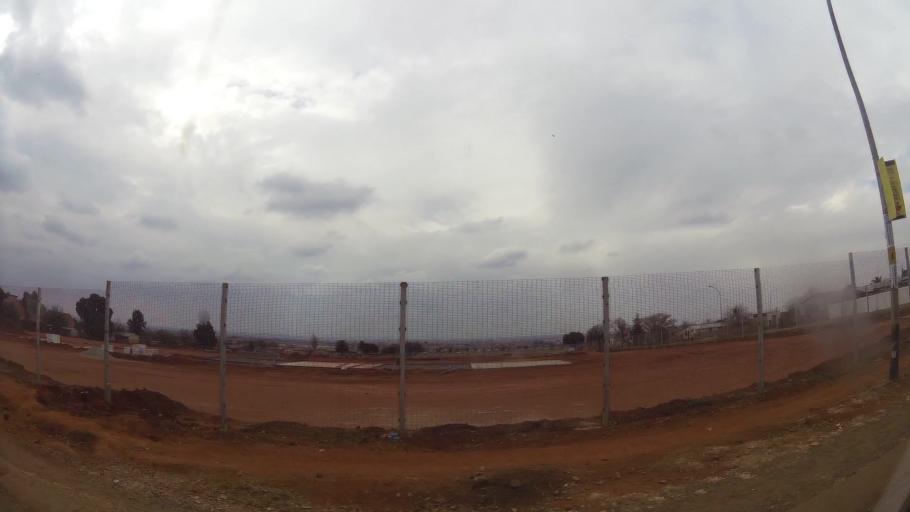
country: ZA
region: Gauteng
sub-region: Ekurhuleni Metropolitan Municipality
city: Germiston
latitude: -26.3899
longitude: 28.1470
